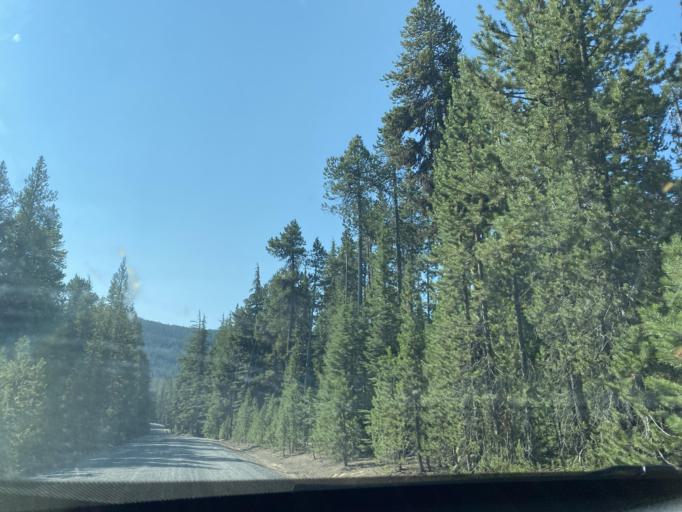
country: US
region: Oregon
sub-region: Deschutes County
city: Three Rivers
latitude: 43.7036
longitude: -121.2742
